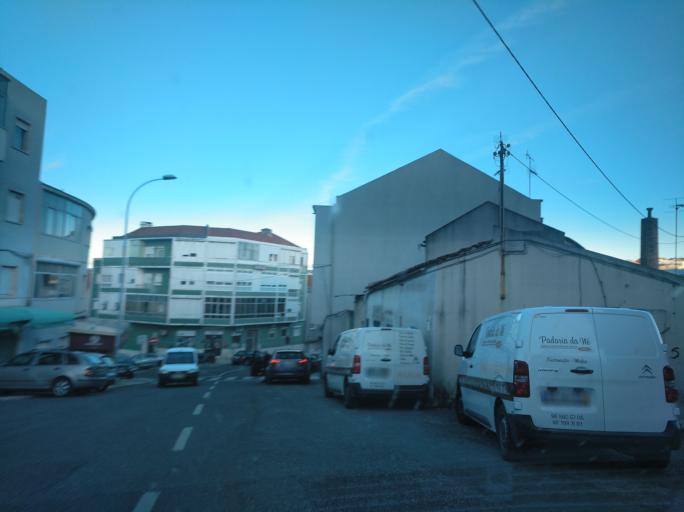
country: PT
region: Lisbon
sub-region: Amadora
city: Amadora
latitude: 38.7473
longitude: -9.2197
